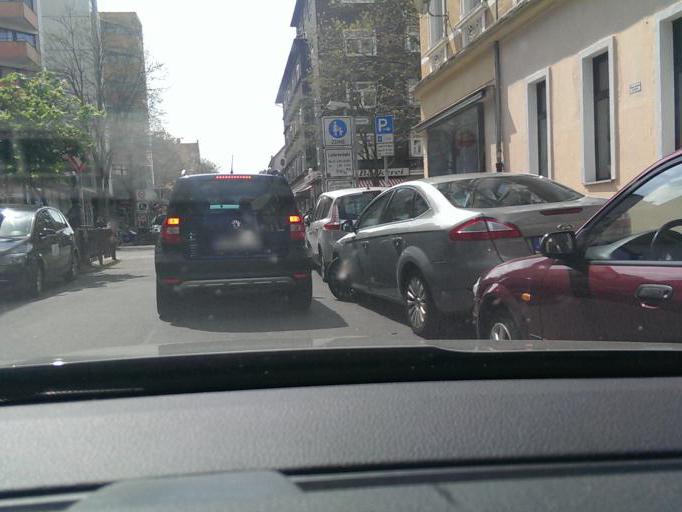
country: DE
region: Lower Saxony
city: Hannover
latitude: 52.3727
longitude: 9.7104
